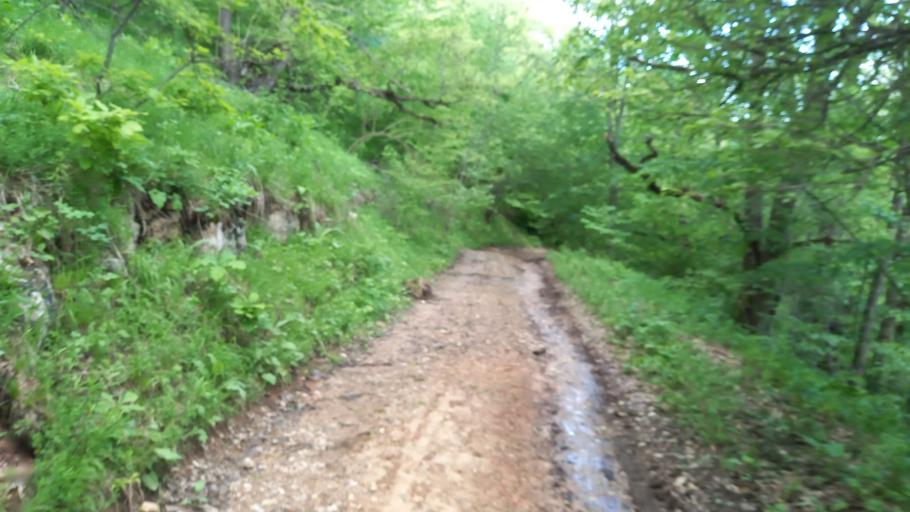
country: RU
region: Adygeya
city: Kamennomostskiy
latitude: 44.2215
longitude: 40.0025
